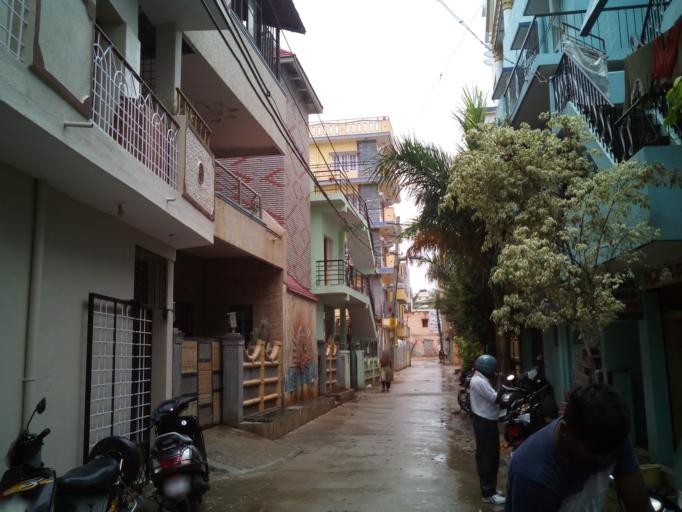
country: IN
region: Karnataka
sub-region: Bangalore Urban
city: Bangalore
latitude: 12.9915
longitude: 77.6638
